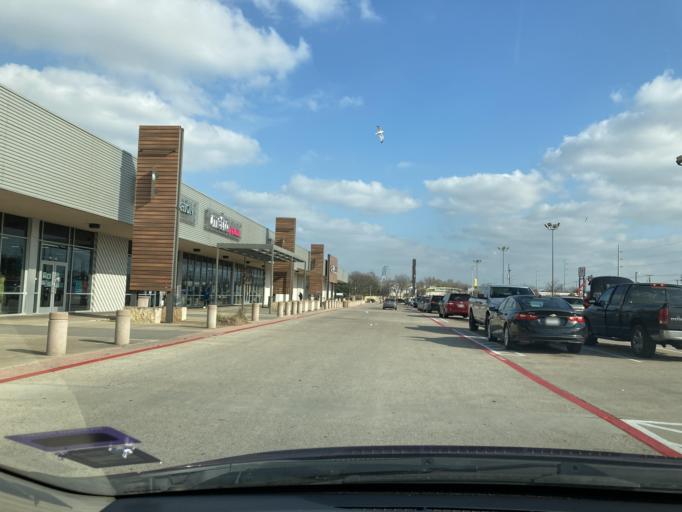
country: US
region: Texas
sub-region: Dallas County
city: Dallas
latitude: 32.7797
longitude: -96.8584
